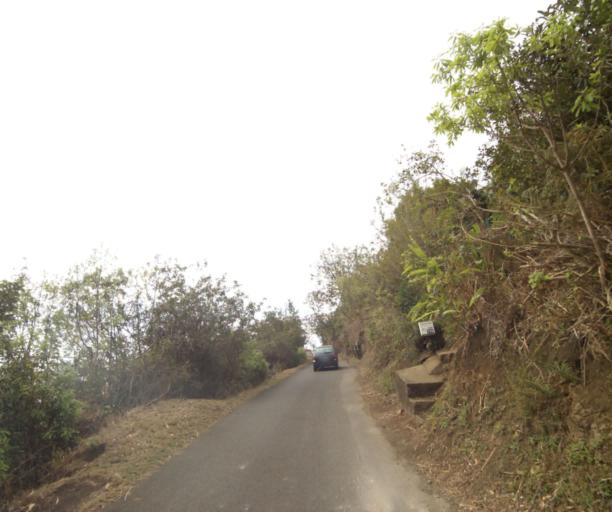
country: RE
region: Reunion
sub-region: Reunion
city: Saint-Paul
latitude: -21.0261
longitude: 55.3051
